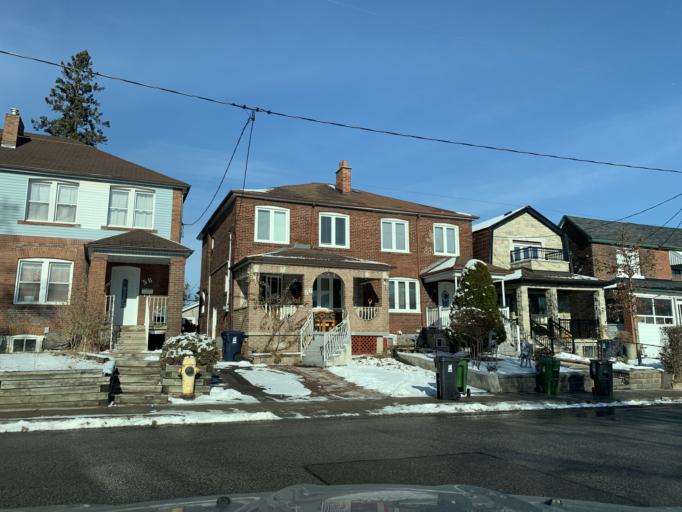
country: CA
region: Ontario
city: Toronto
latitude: 43.6783
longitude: -79.4763
